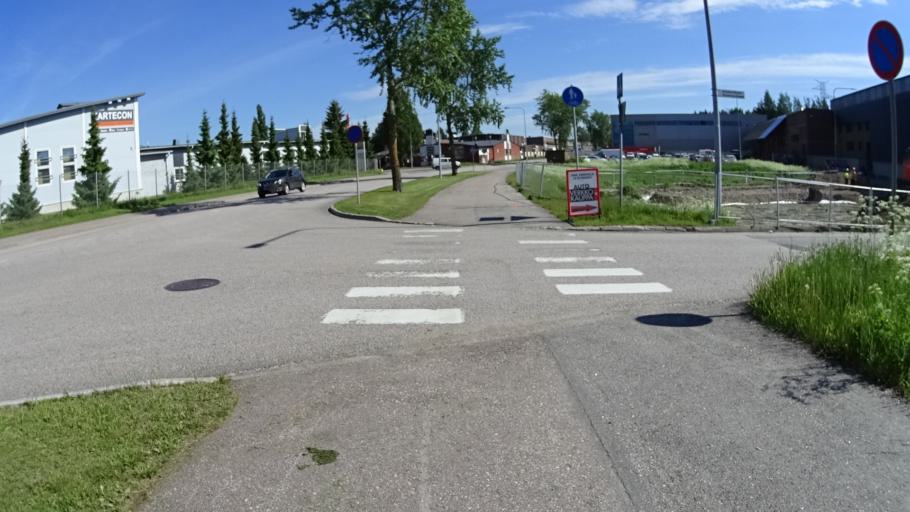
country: FI
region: Uusimaa
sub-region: Helsinki
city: Kilo
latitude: 60.2793
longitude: 24.8147
